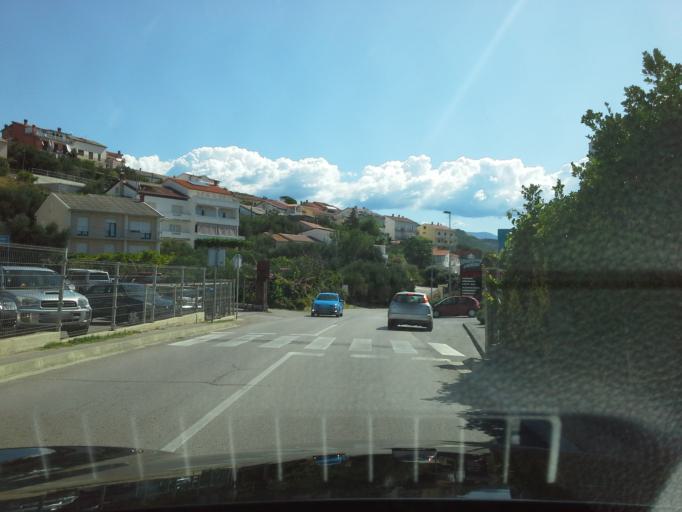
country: HR
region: Primorsko-Goranska
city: Banjol
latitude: 44.7604
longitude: 14.7663
